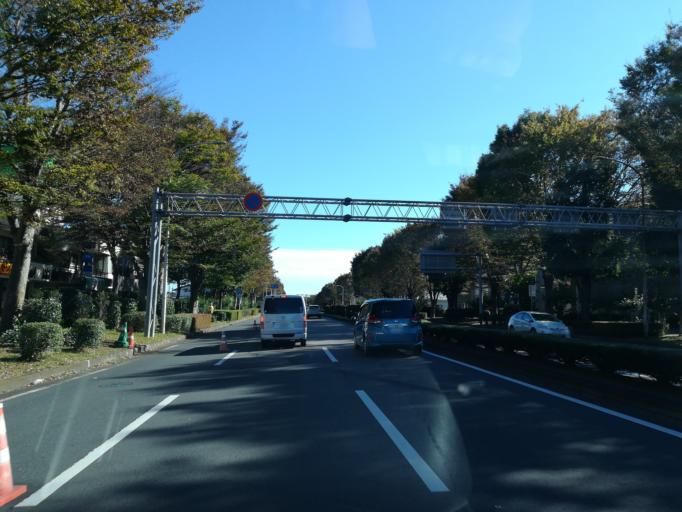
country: JP
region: Ibaraki
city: Naka
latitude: 36.0782
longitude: 140.1096
